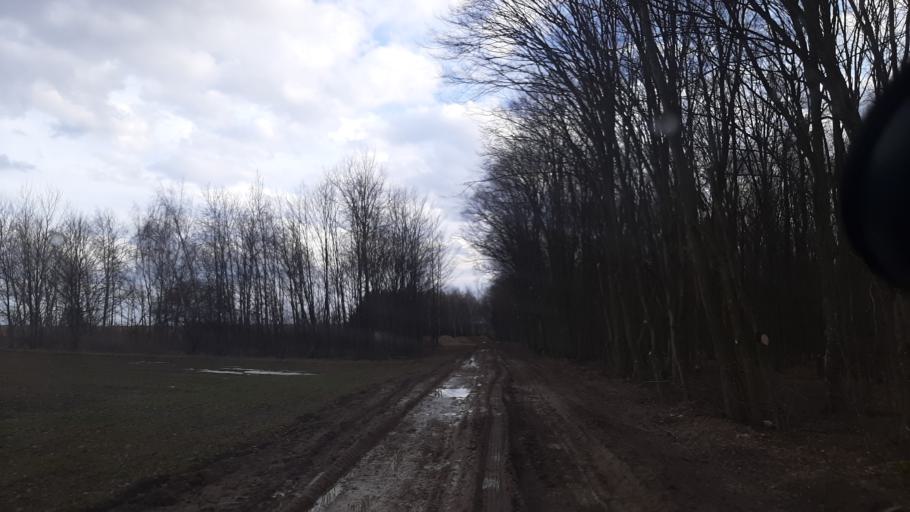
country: PL
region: Lublin Voivodeship
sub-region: Powiat lubelski
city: Jastkow
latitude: 51.3714
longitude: 22.4167
